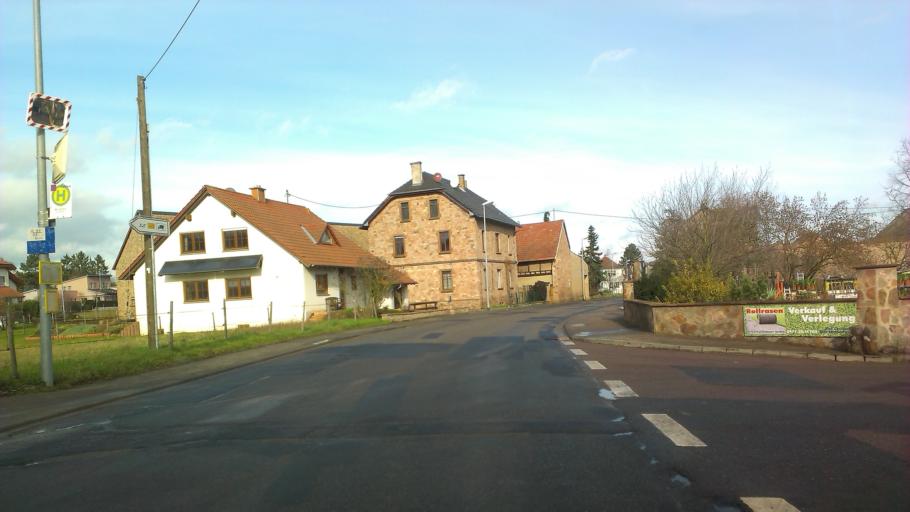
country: DE
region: Rheinland-Pfalz
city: Neu-Bamberg
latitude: 49.7938
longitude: 7.9206
